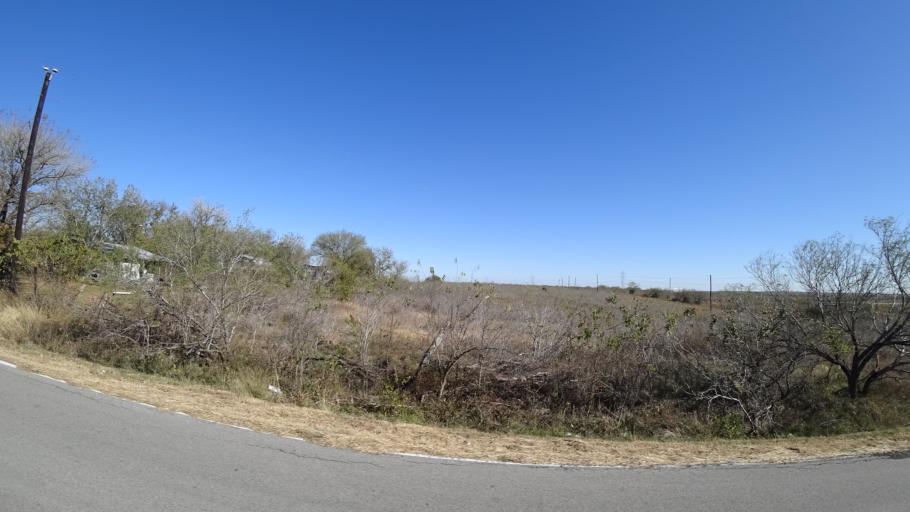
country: US
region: Texas
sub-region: Travis County
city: Onion Creek
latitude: 30.1044
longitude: -97.6712
